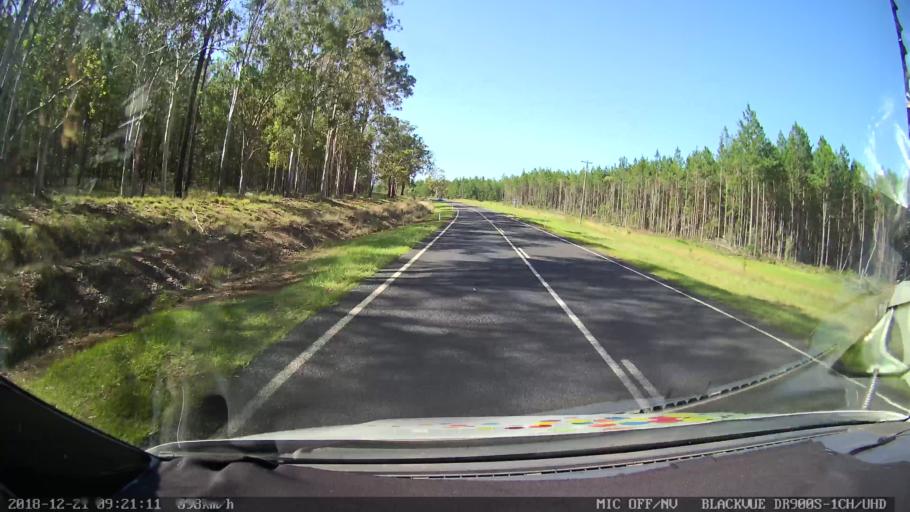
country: AU
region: New South Wales
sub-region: Clarence Valley
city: Maclean
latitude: -29.3255
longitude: 152.9978
